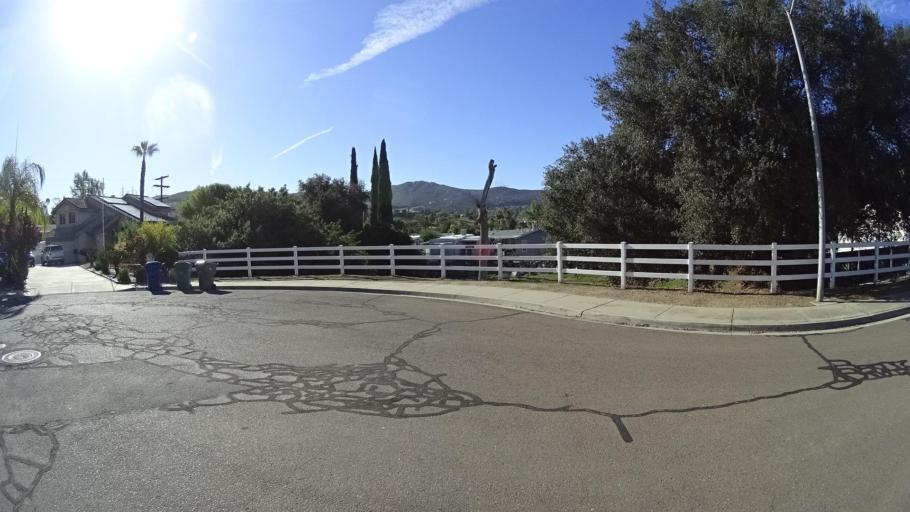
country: US
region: California
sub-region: San Diego County
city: Lakeside
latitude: 32.8442
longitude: -116.8895
